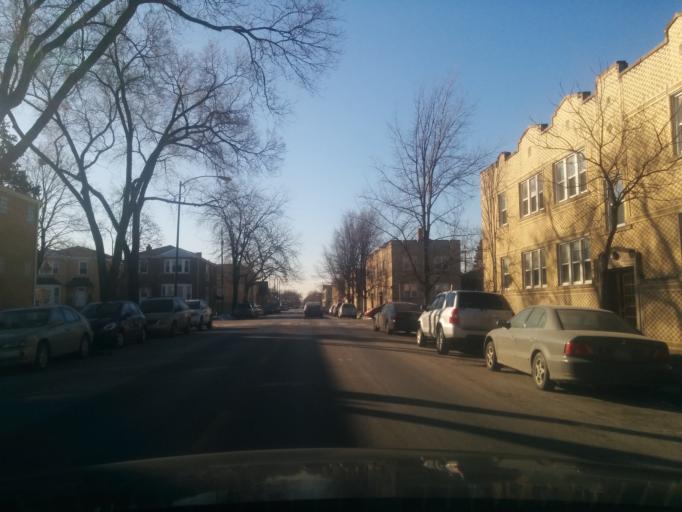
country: US
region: Illinois
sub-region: Cook County
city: Elmwood Park
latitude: 41.9410
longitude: -87.7568
